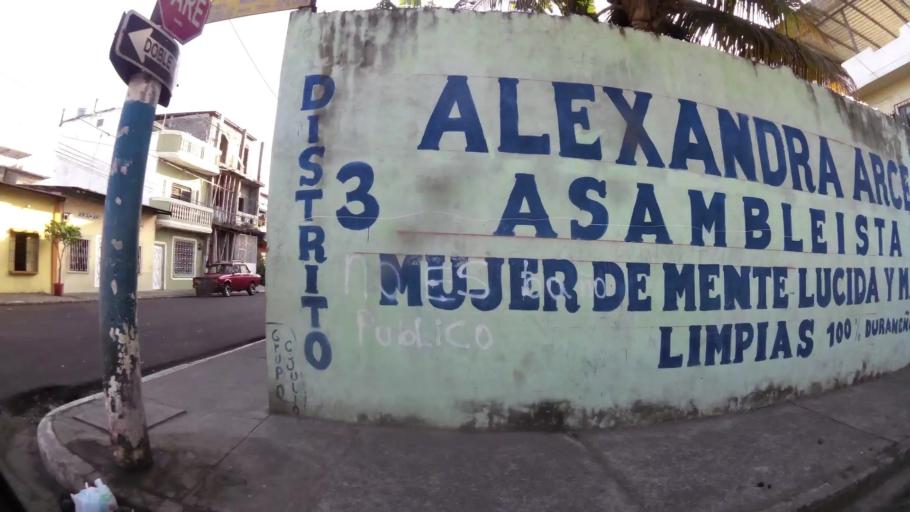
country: EC
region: Guayas
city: Eloy Alfaro
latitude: -2.1671
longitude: -79.8492
